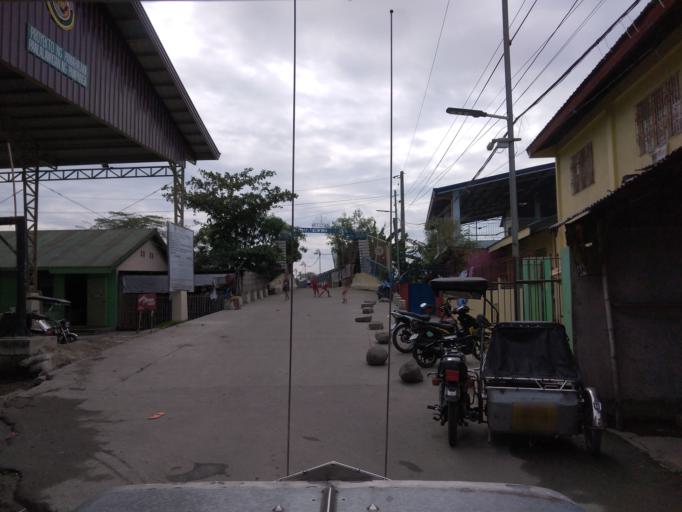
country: PH
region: Central Luzon
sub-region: Province of Pampanga
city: Sexmoan
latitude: 14.9328
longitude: 120.6256
